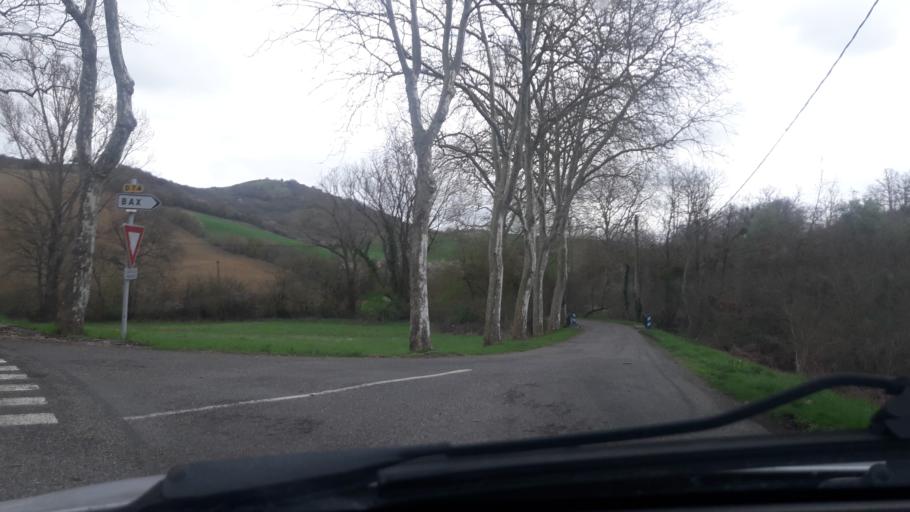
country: FR
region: Midi-Pyrenees
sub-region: Departement de la Haute-Garonne
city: Montesquieu-Volvestre
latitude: 43.2319
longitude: 1.2845
